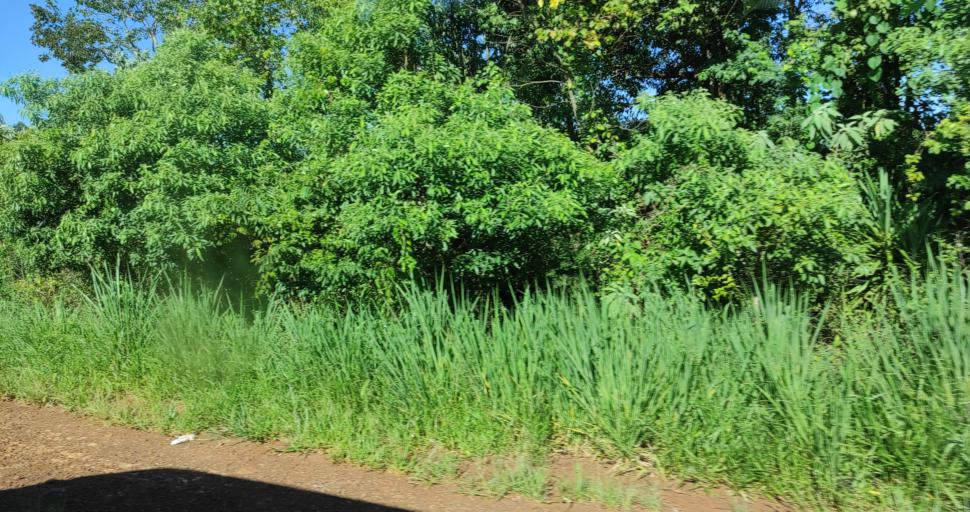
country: AR
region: Misiones
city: El Soberbio
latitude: -27.1884
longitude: -54.1063
